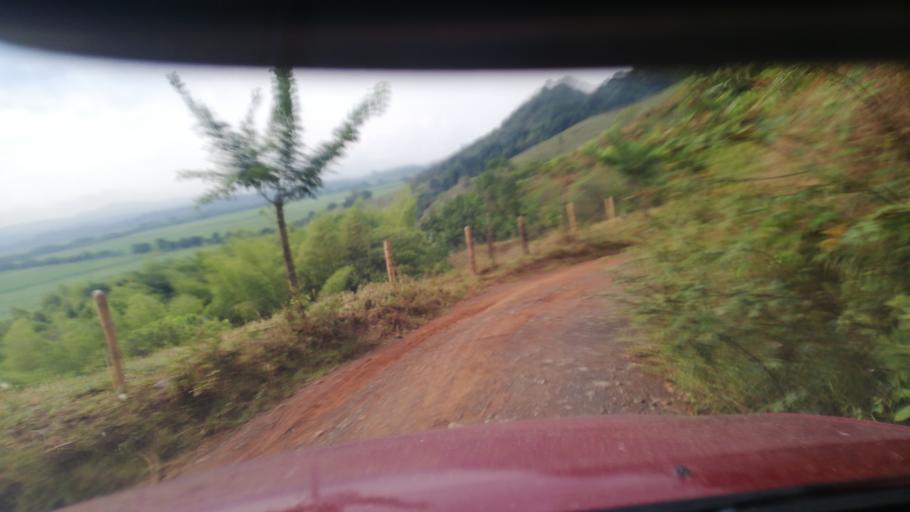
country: CO
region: Risaralda
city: La Virginia
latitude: 4.8798
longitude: -75.9351
